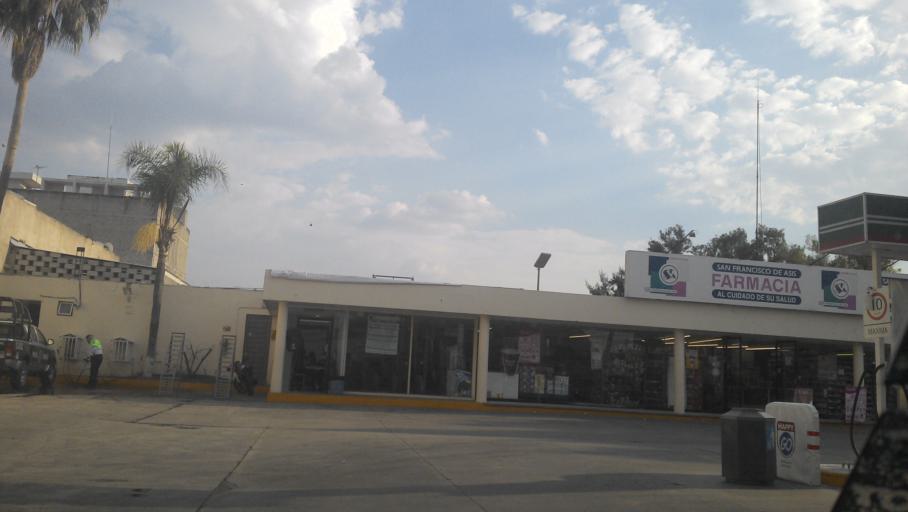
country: MX
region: Guanajuato
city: San Francisco del Rincon
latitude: 21.0209
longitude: -101.8515
